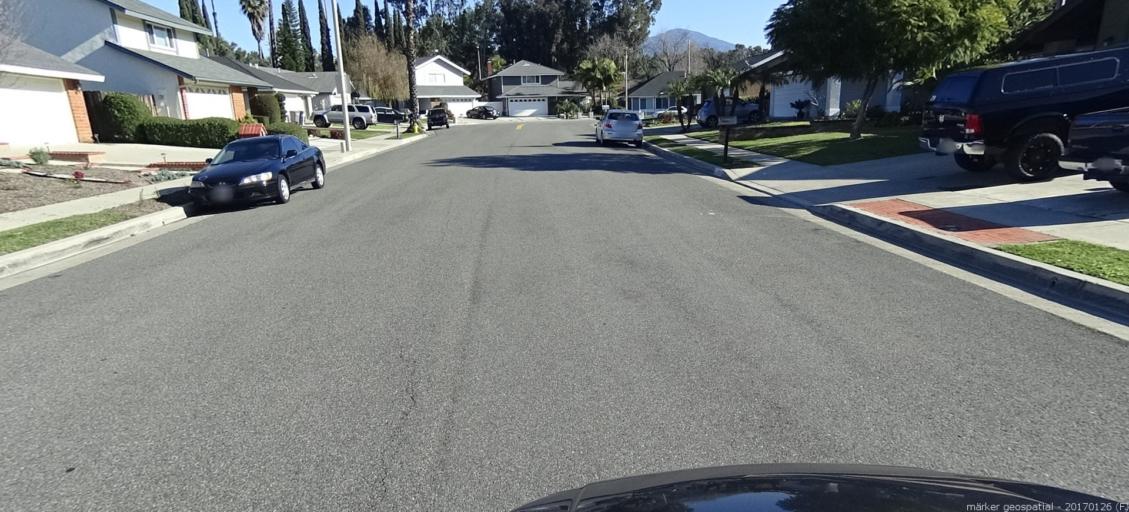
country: US
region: California
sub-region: Orange County
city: Lake Forest
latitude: 33.6357
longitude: -117.6808
